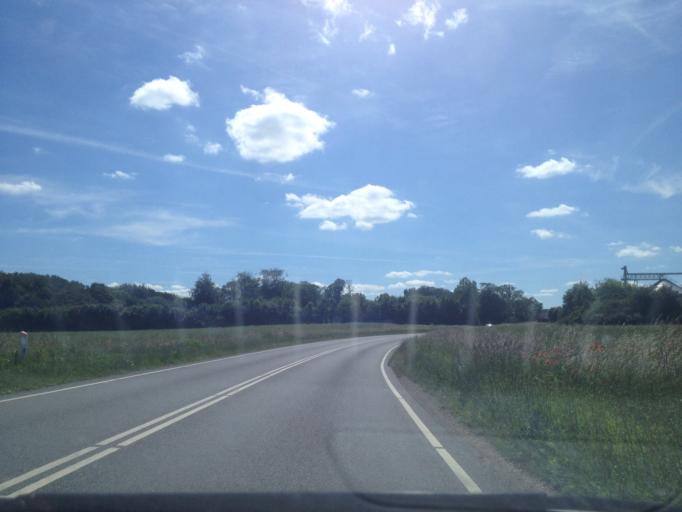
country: DK
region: Zealand
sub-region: Odsherred Kommune
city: Horve
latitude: 55.7376
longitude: 11.3682
